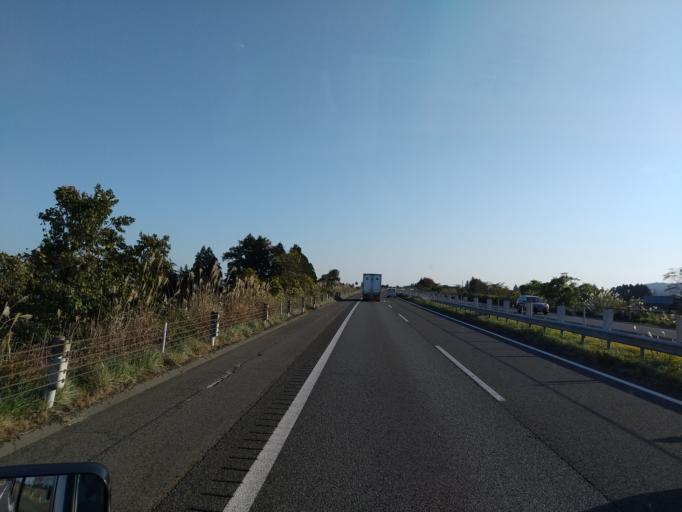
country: JP
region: Iwate
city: Morioka-shi
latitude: 39.5811
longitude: 141.1195
